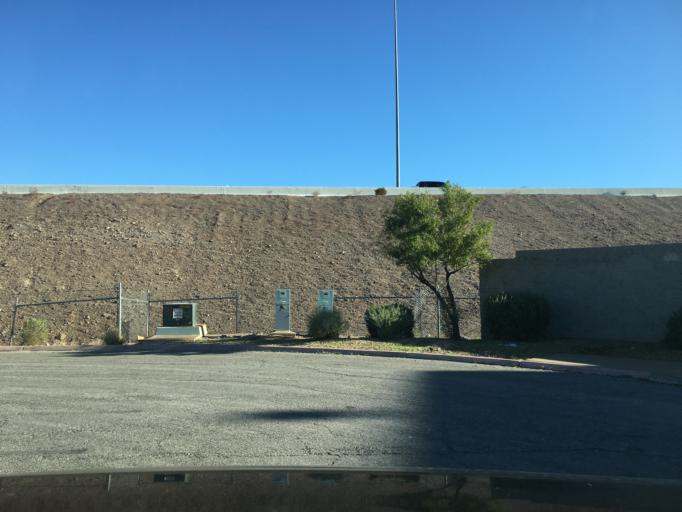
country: US
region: Nevada
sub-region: Clark County
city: Henderson
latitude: 36.0385
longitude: -115.0206
